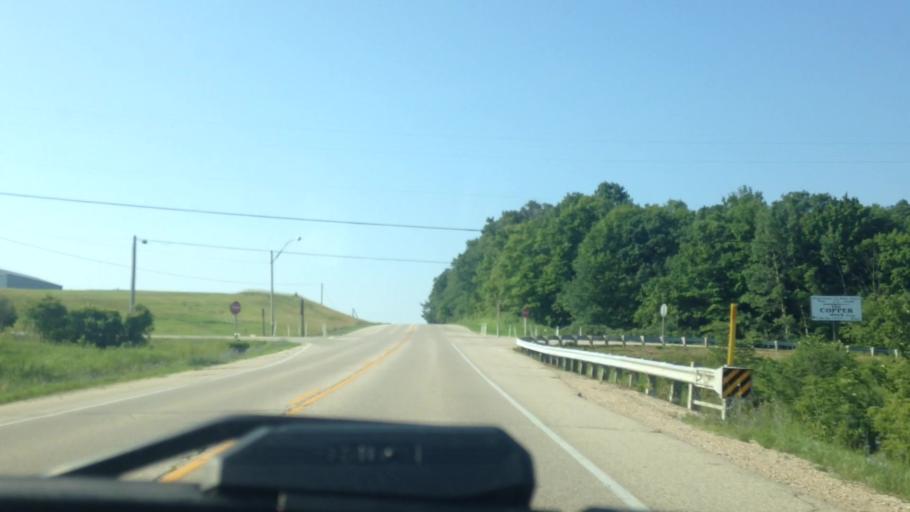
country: US
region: Wisconsin
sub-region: Washington County
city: Richfield
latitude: 43.2376
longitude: -88.2619
